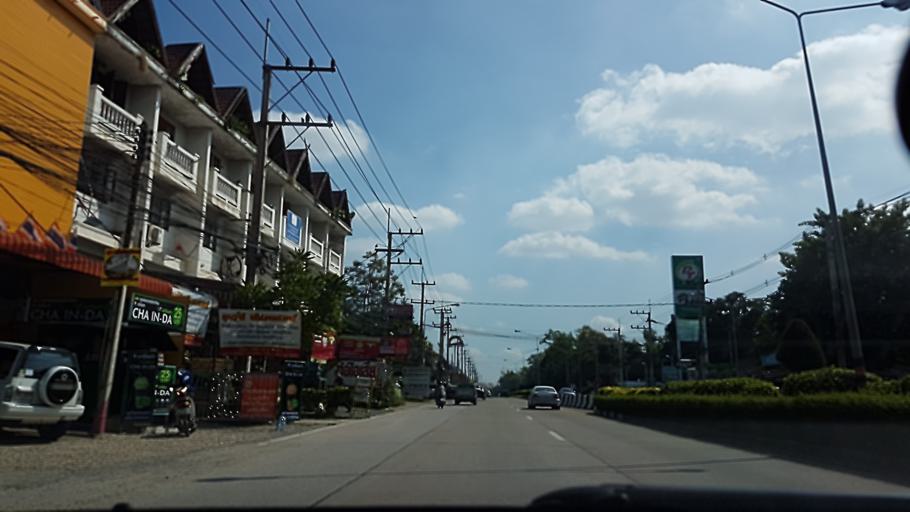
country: TH
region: Chiang Mai
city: Chiang Mai
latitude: 18.8353
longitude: 98.9757
